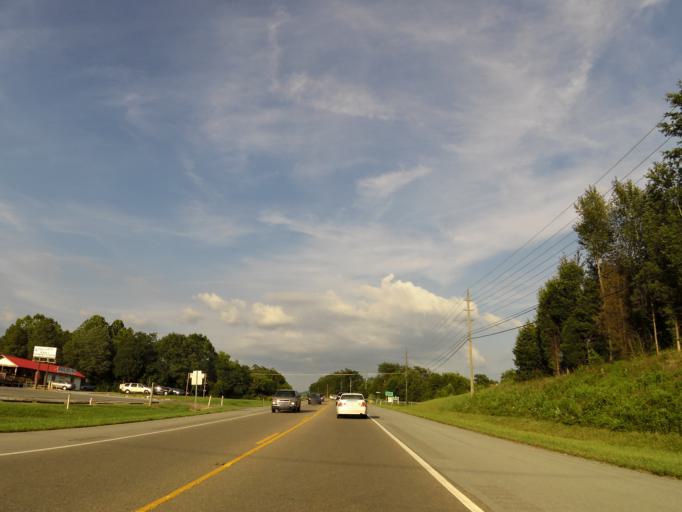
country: US
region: Tennessee
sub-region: Sevier County
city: Sevierville
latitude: 35.8832
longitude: -83.4614
